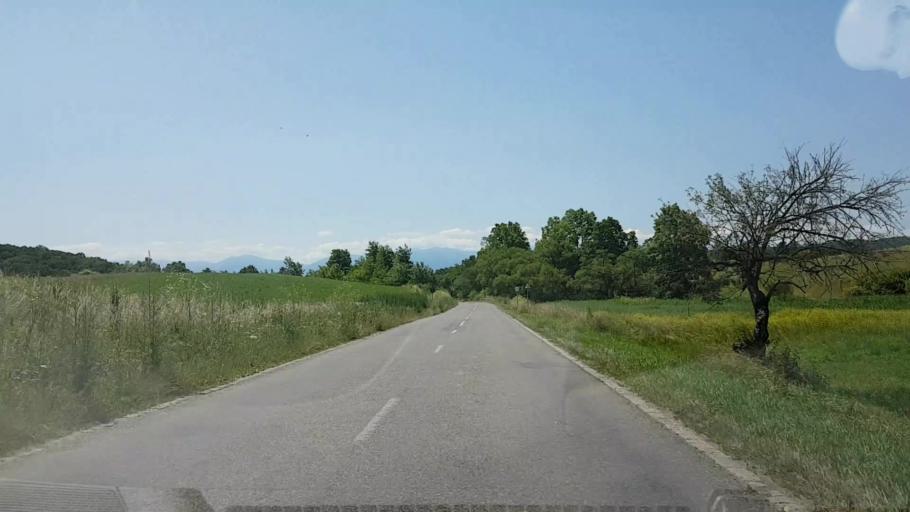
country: RO
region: Brasov
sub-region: Comuna Cincu
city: Cincu
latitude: 45.8938
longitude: 24.8115
